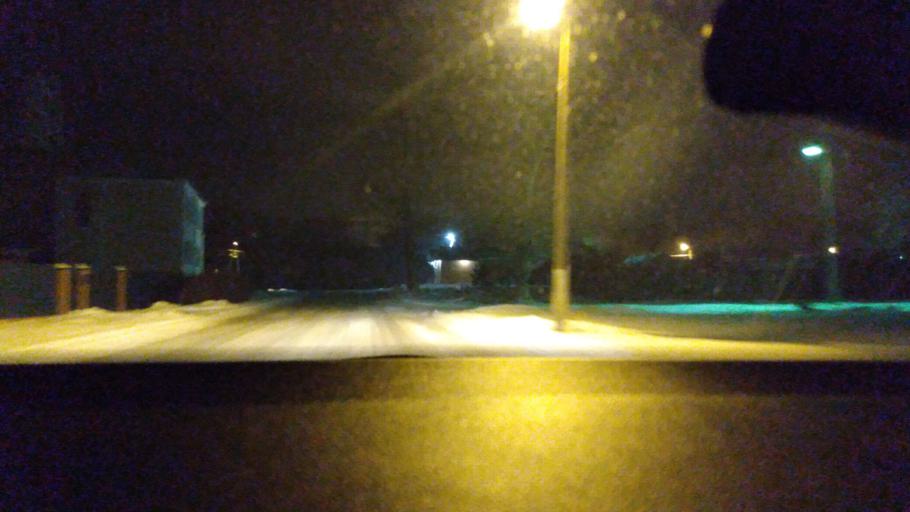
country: RU
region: Moskovskaya
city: Krasnaya Poyma
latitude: 55.0547
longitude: 39.1197
